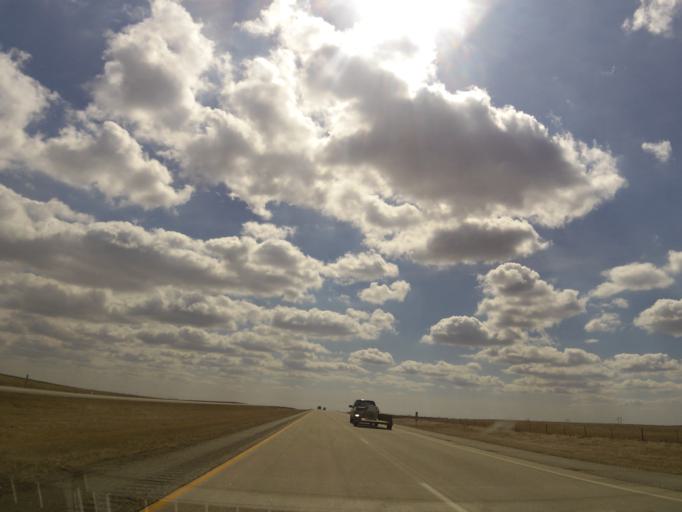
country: US
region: South Dakota
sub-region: Codington County
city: Watertown
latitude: 45.2527
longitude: -97.0518
